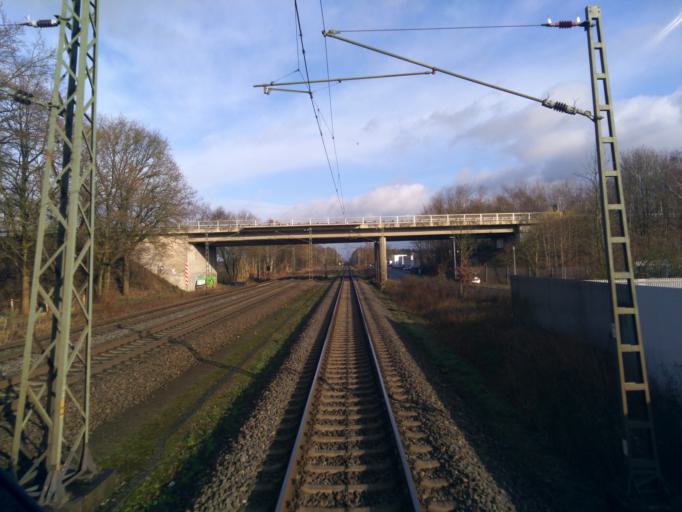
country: DE
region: Lower Saxony
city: Rotenburg
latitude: 53.1252
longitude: 9.4269
